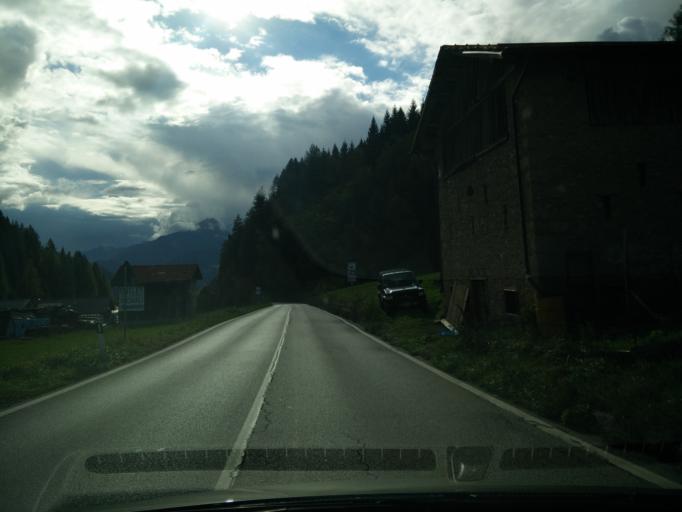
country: IT
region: Veneto
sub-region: Provincia di Belluno
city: Domegge di Cadore
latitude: 46.4662
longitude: 12.4256
